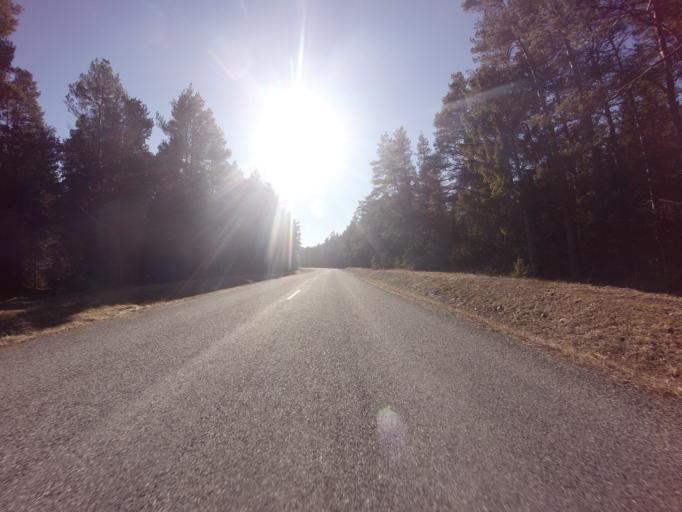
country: EE
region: Saare
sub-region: Kuressaare linn
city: Kuressaare
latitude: 58.5158
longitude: 22.3227
